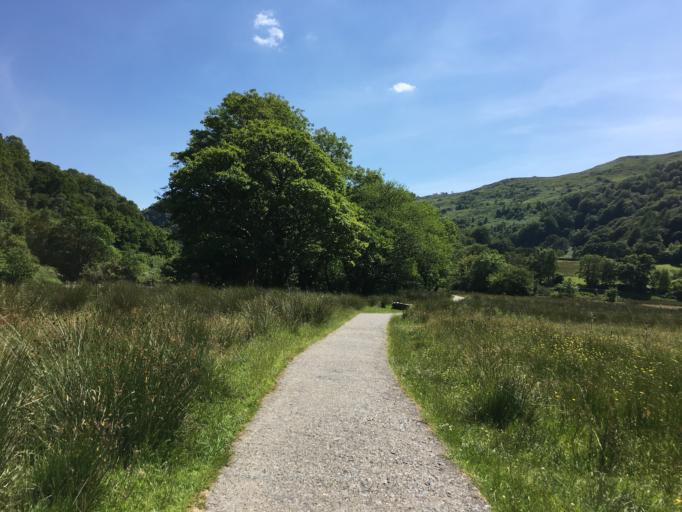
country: GB
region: Wales
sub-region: Gwynedd
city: Penrhyndeudraeth
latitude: 53.0075
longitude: -4.1003
